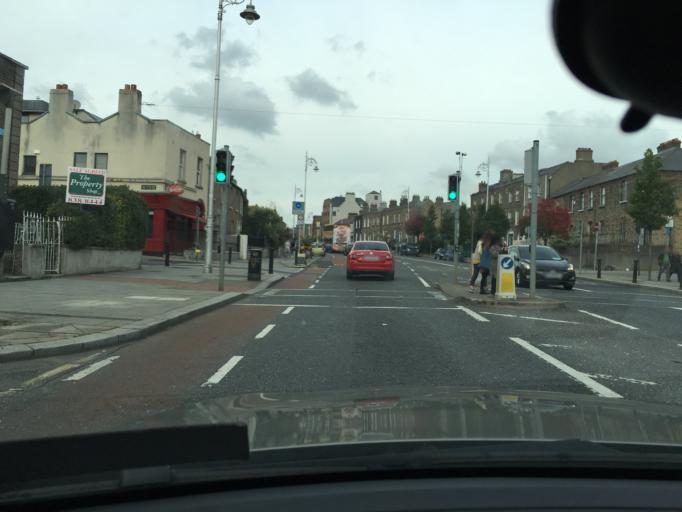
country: IE
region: Leinster
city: Cabra
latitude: 53.3522
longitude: -6.2836
